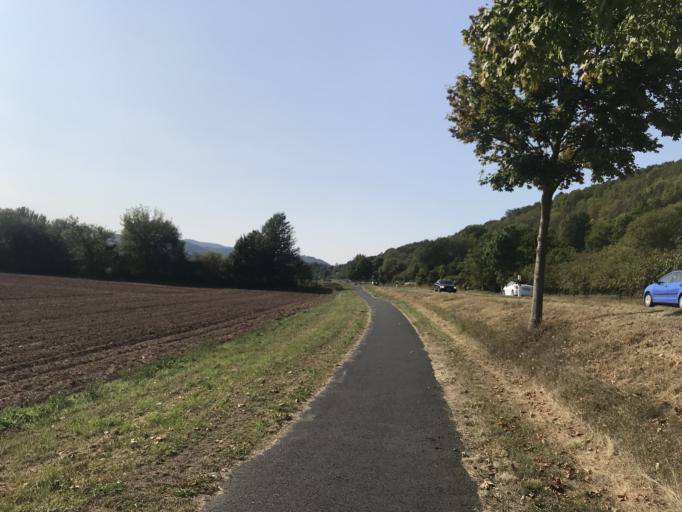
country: DE
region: Thuringia
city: Treffurt
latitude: 51.1371
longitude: 10.2189
